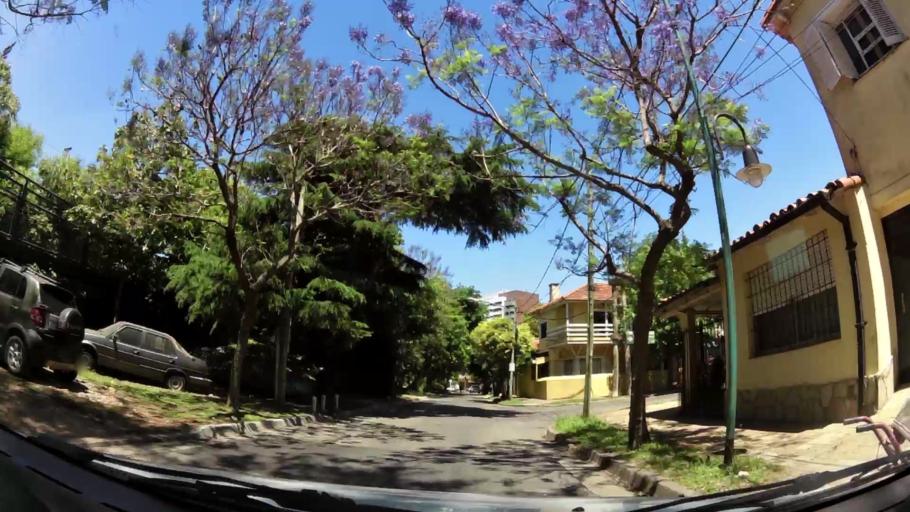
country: AR
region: Buenos Aires
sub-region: Partido de Vicente Lopez
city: Olivos
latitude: -34.5002
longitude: -58.4818
